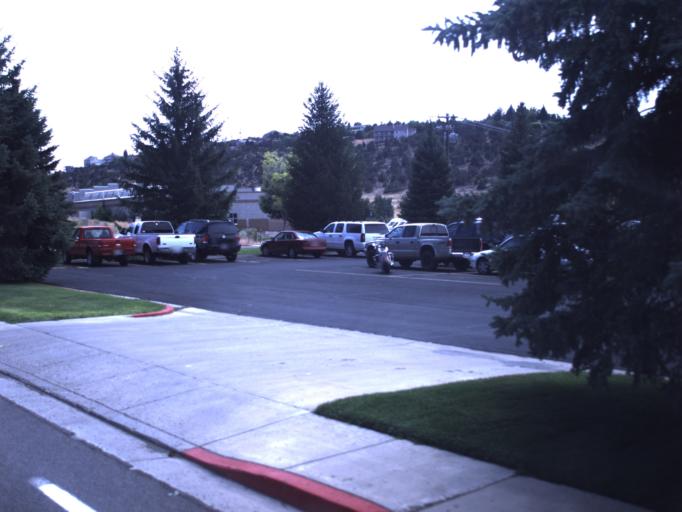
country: US
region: Utah
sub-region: Iron County
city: Cedar City
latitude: 37.6746
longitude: -113.0780
